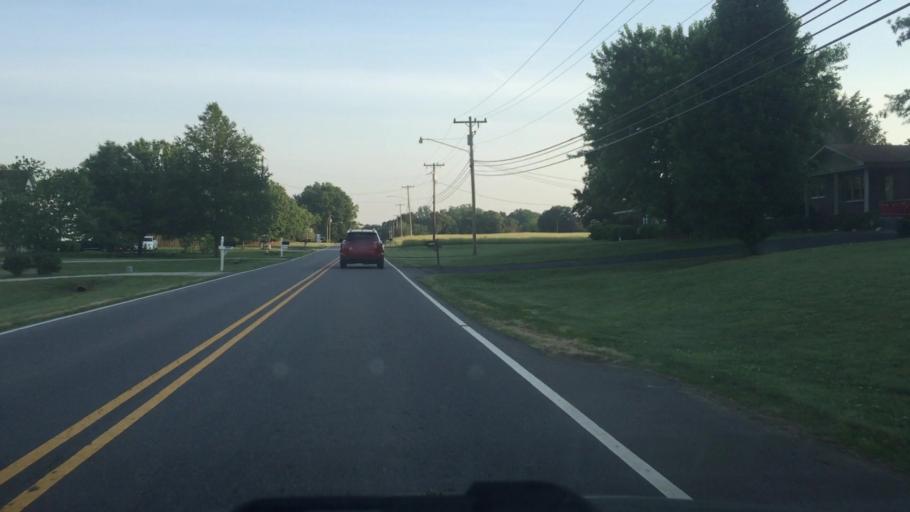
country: US
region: North Carolina
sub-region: Rockingham County
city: Reidsville
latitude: 36.3475
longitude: -79.6993
